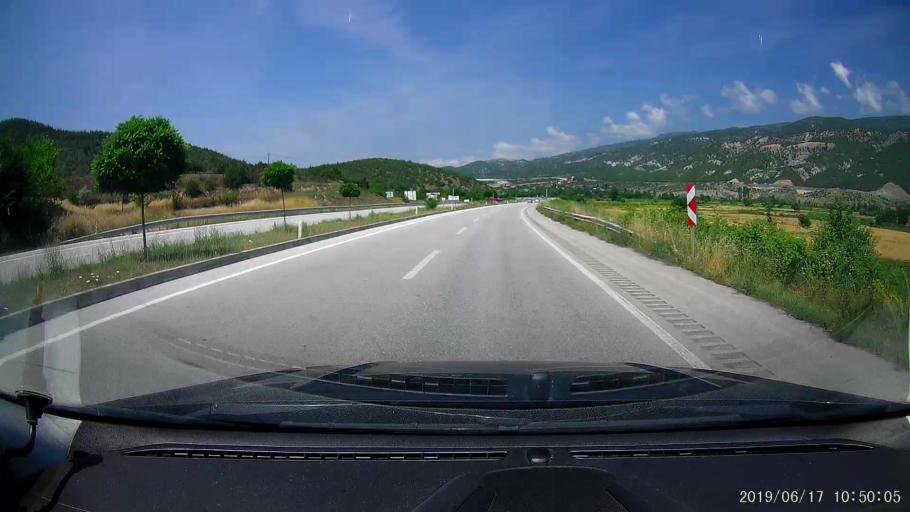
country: TR
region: Corum
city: Hacihamza
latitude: 41.0976
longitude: 34.3936
